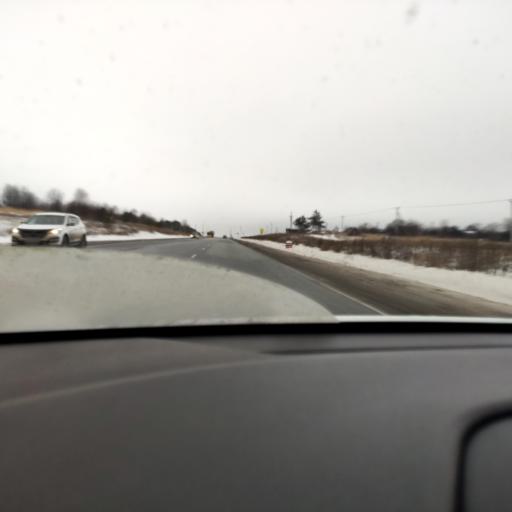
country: RU
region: Tatarstan
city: Verkhniy Uslon
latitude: 55.7221
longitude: 48.8315
